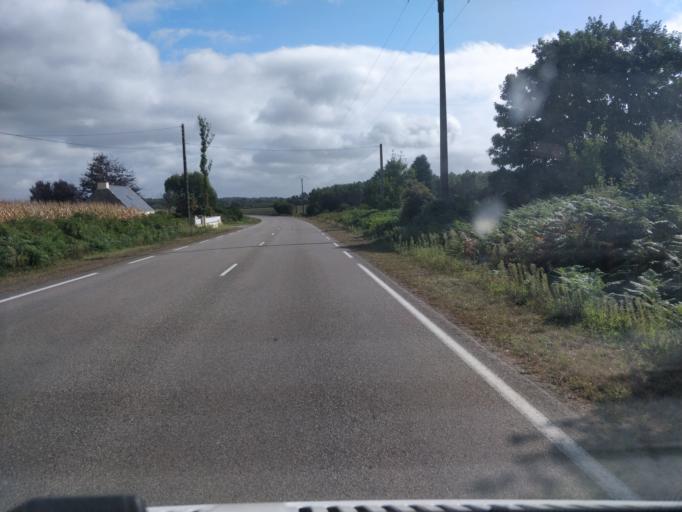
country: FR
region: Brittany
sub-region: Departement du Finistere
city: Plozevet
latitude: 47.9955
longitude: -4.3813
